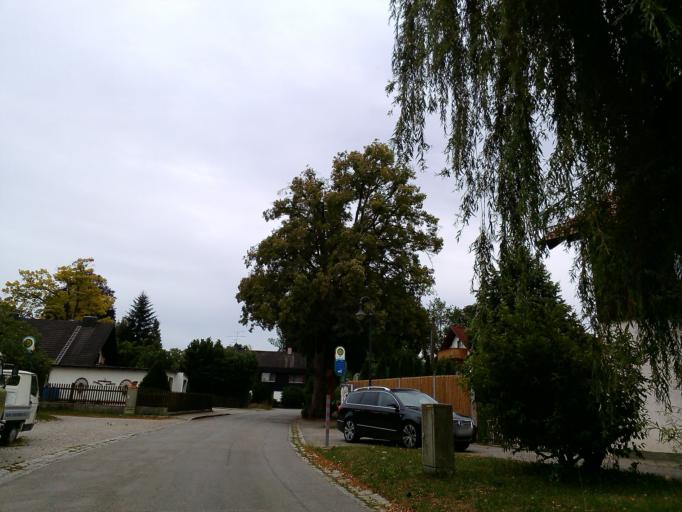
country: DE
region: Bavaria
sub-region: Upper Bavaria
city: Gauting
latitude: 48.0789
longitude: 11.3437
